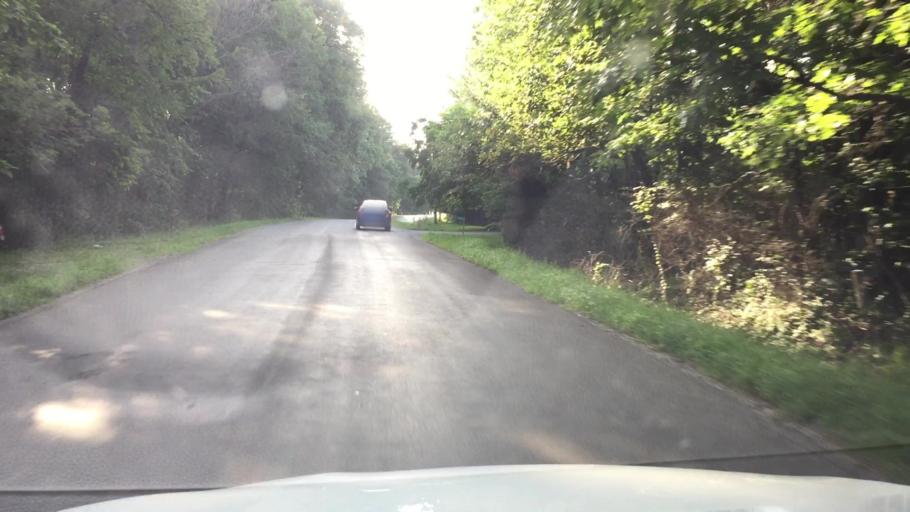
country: US
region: Iowa
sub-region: Linn County
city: Ely
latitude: 41.8300
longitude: -91.6275
